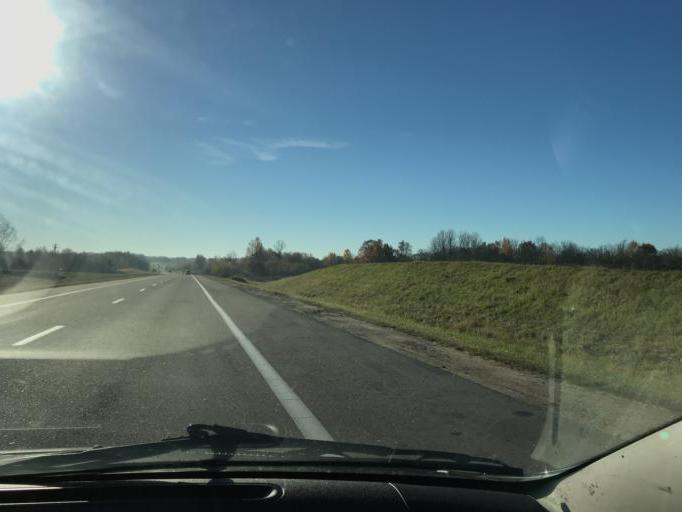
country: BY
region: Vitebsk
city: Vitebsk
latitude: 55.1018
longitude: 30.2974
